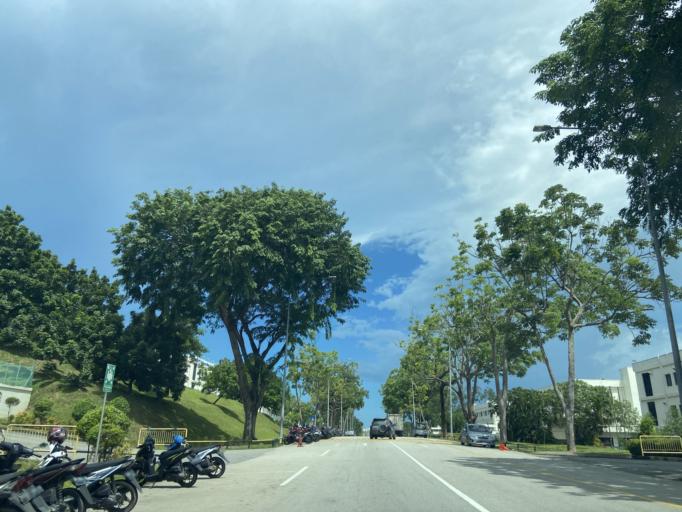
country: SG
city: Singapore
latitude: 1.0661
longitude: 104.0293
